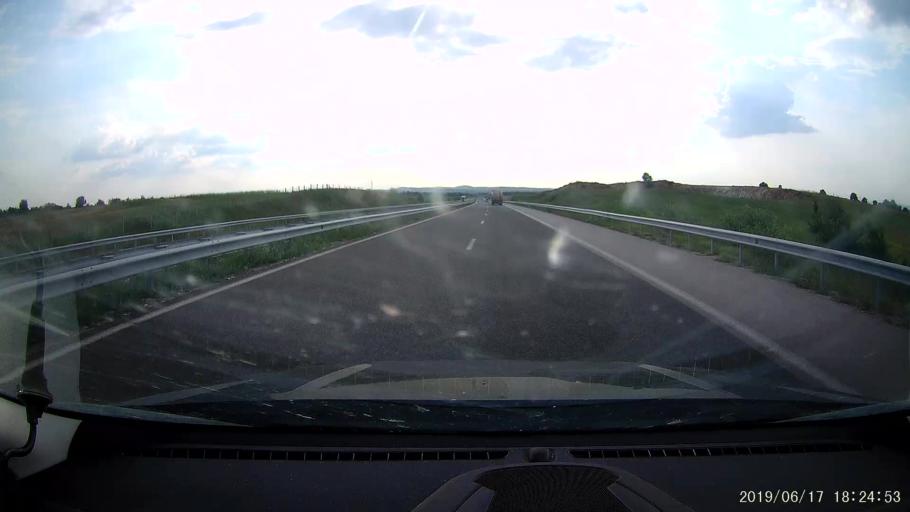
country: BG
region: Khaskovo
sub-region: Obshtina Dimitrovgrad
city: Dimitrovgrad
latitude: 41.9884
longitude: 25.6779
